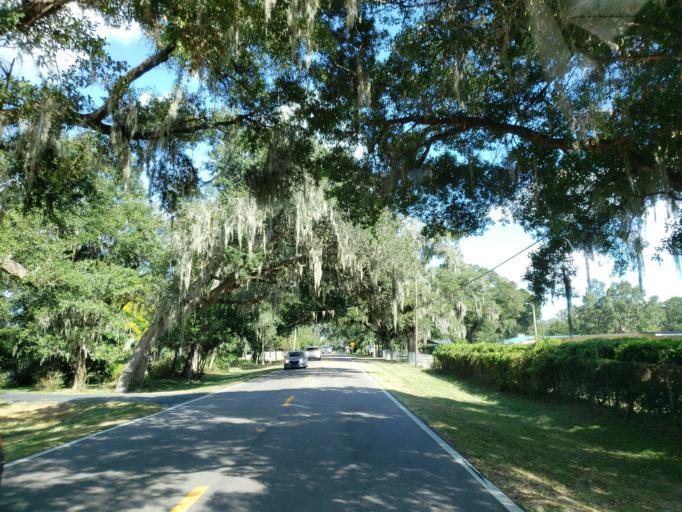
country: US
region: Florida
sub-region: Hillsborough County
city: Bloomingdale
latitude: 27.9083
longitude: -82.2223
